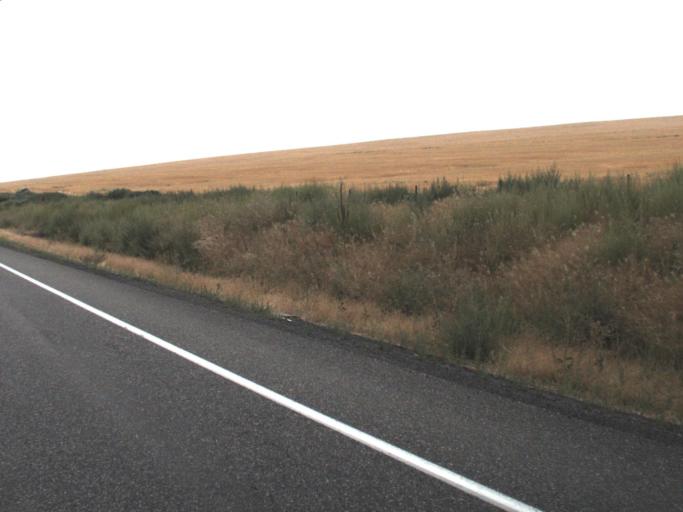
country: US
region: Washington
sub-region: Benton County
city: Prosser
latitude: 46.2005
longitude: -119.7058
